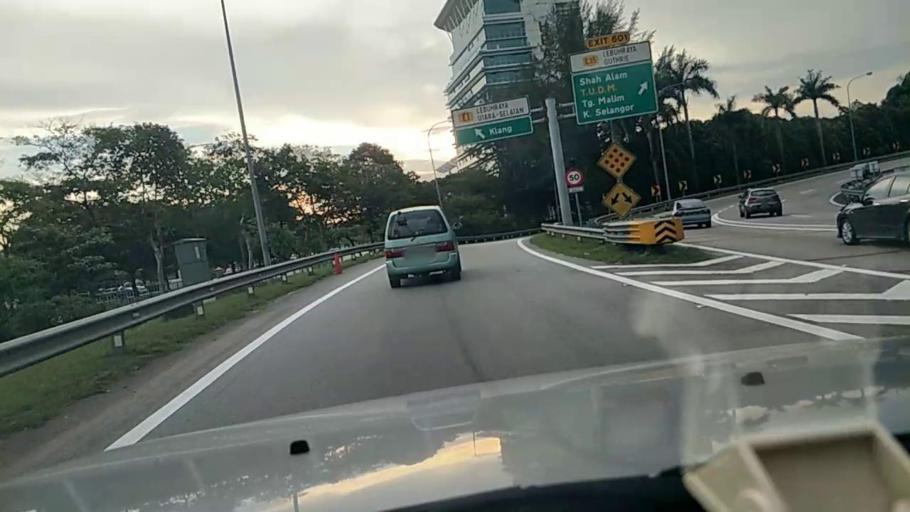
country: MY
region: Selangor
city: Shah Alam
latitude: 3.0910
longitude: 101.5475
